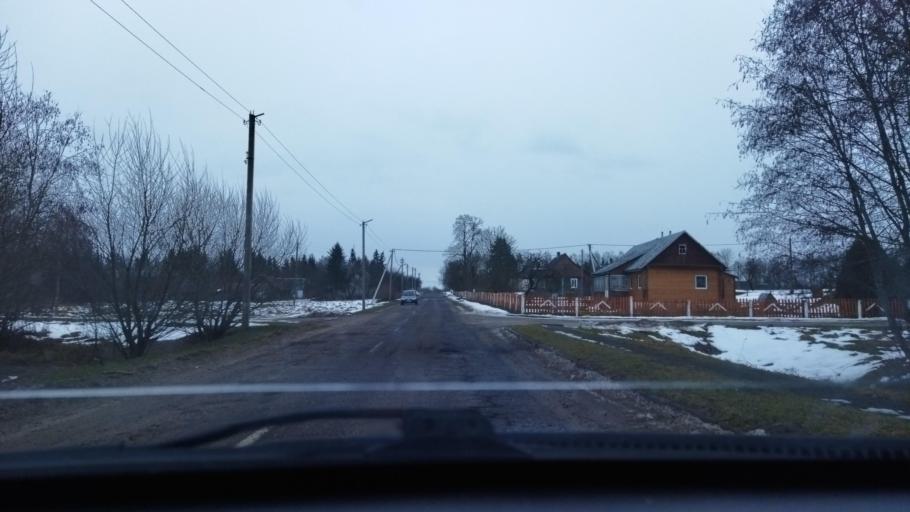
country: BY
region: Minsk
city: Svir
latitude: 54.8989
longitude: 26.4025
